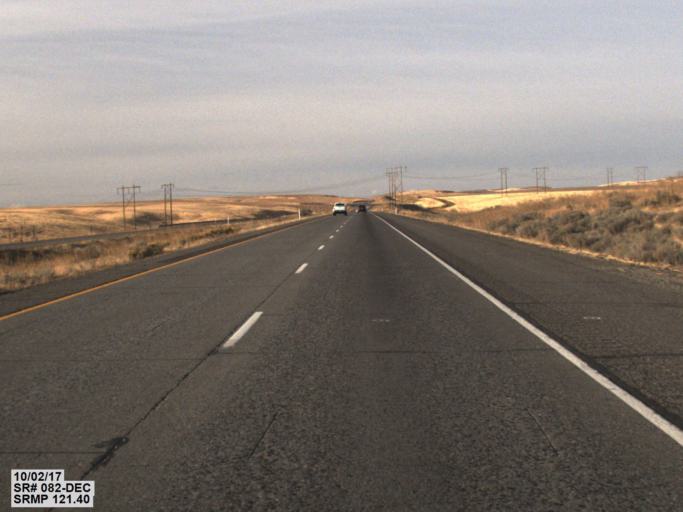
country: US
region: Washington
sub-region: Benton County
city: Highland
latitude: 46.0449
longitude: -119.2241
